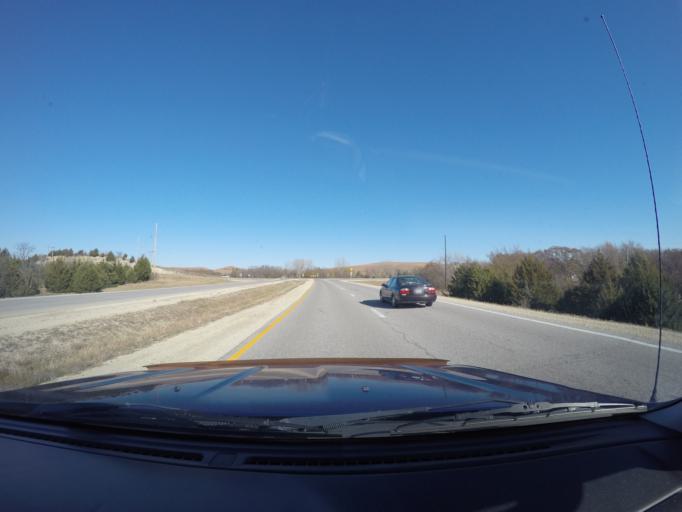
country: US
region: Kansas
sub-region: Riley County
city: Manhattan
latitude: 39.2456
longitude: -96.6229
